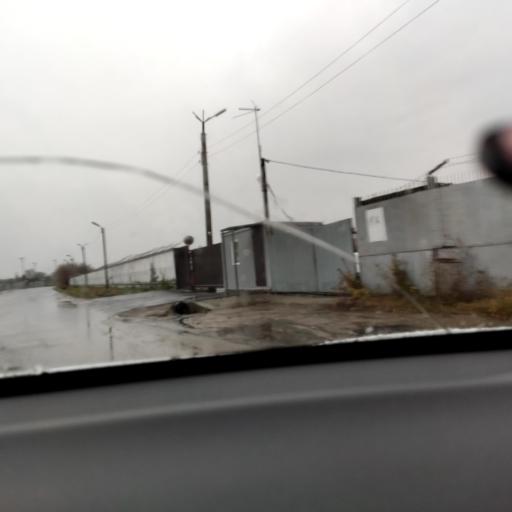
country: RU
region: Tatarstan
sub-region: Gorod Kazan'
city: Kazan
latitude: 55.8649
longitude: 49.1090
